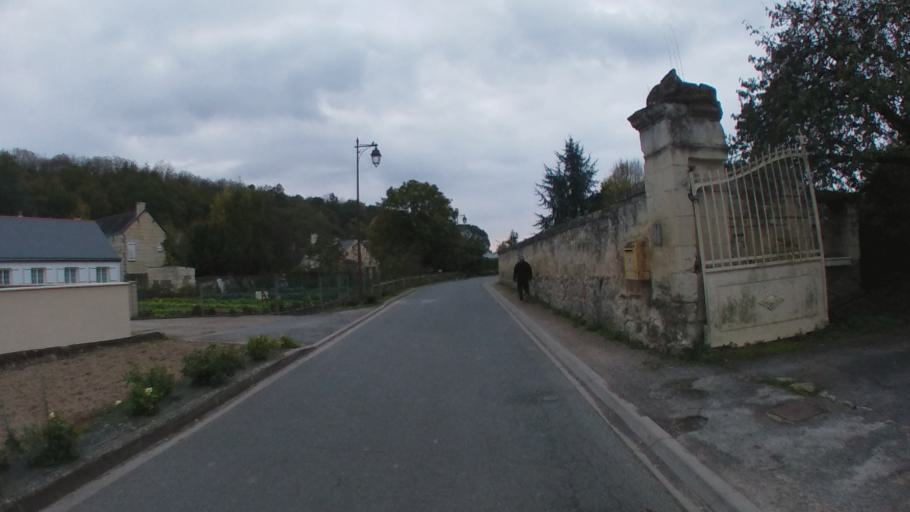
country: FR
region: Pays de la Loire
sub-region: Departement de Maine-et-Loire
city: Distre
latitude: 47.2487
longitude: -0.1458
